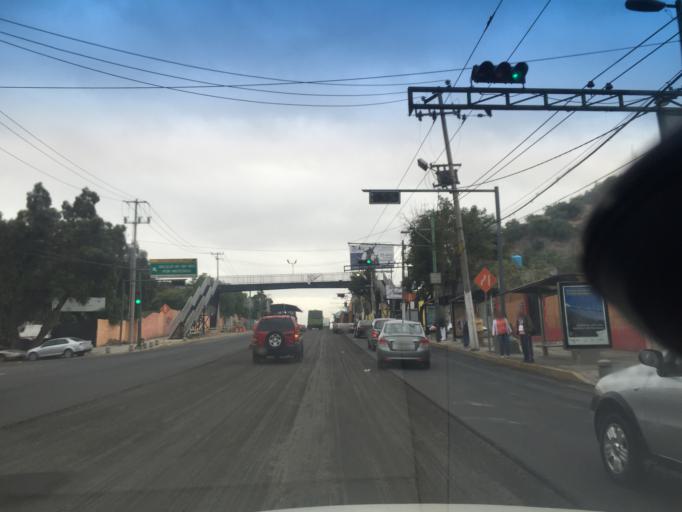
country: MX
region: Mexico City
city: Gustavo A. Madero
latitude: 19.4877
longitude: -99.1133
